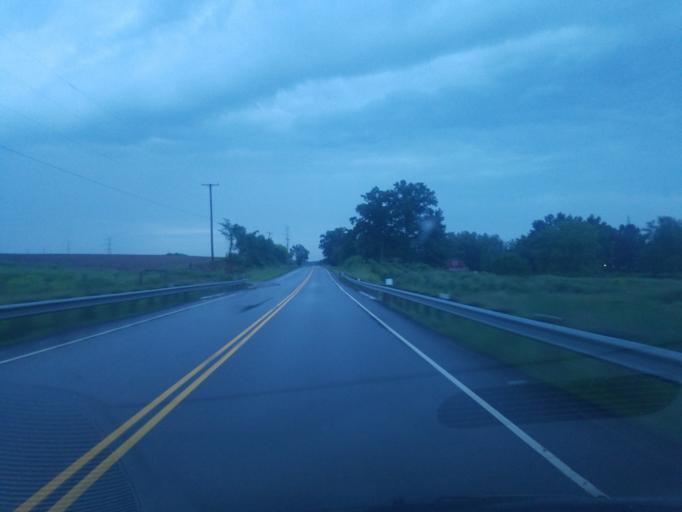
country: US
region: Ohio
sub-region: Mahoning County
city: Canfield
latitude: 40.9795
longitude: -80.7560
